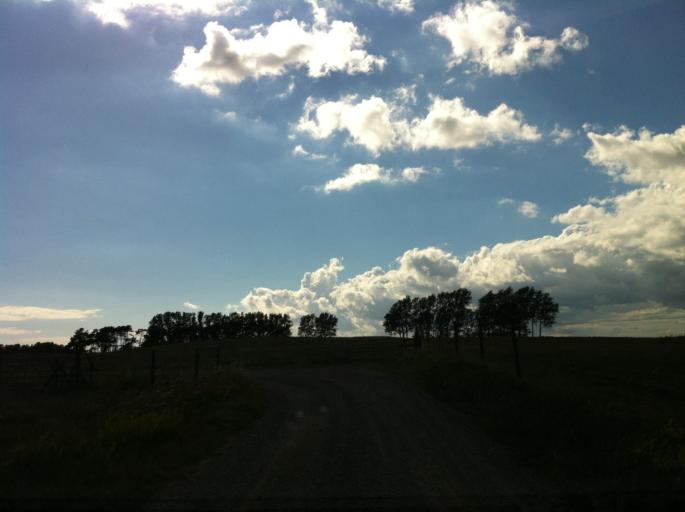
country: SE
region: Skane
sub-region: Ystads Kommun
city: Kopingebro
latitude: 55.3910
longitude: 14.0506
